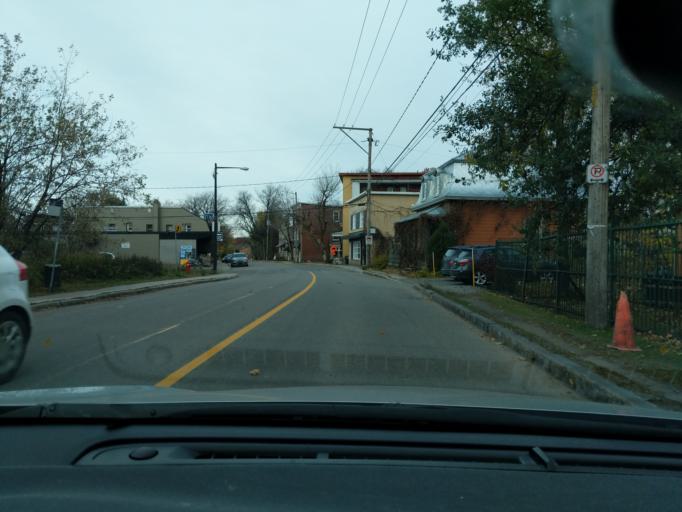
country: CA
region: Quebec
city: Quebec
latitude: 46.7808
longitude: -71.2475
